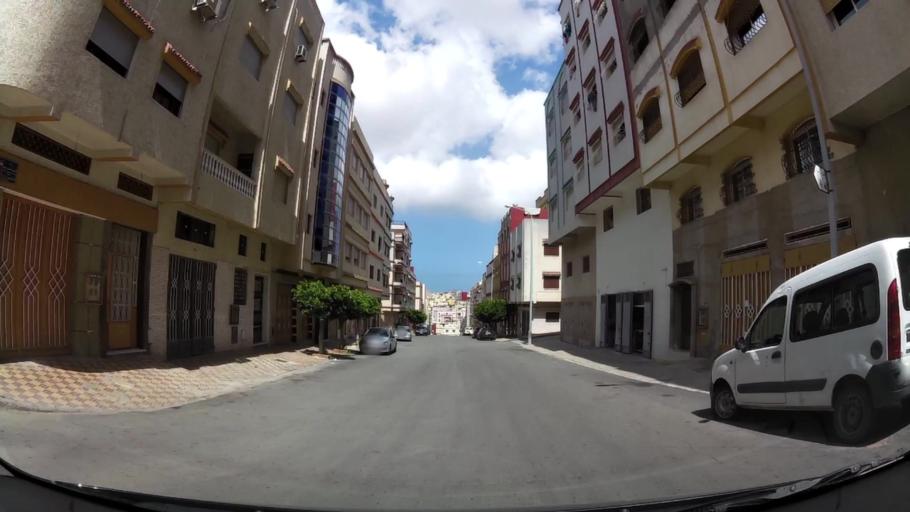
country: MA
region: Tanger-Tetouan
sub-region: Tanger-Assilah
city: Tangier
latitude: 35.7559
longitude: -5.8280
